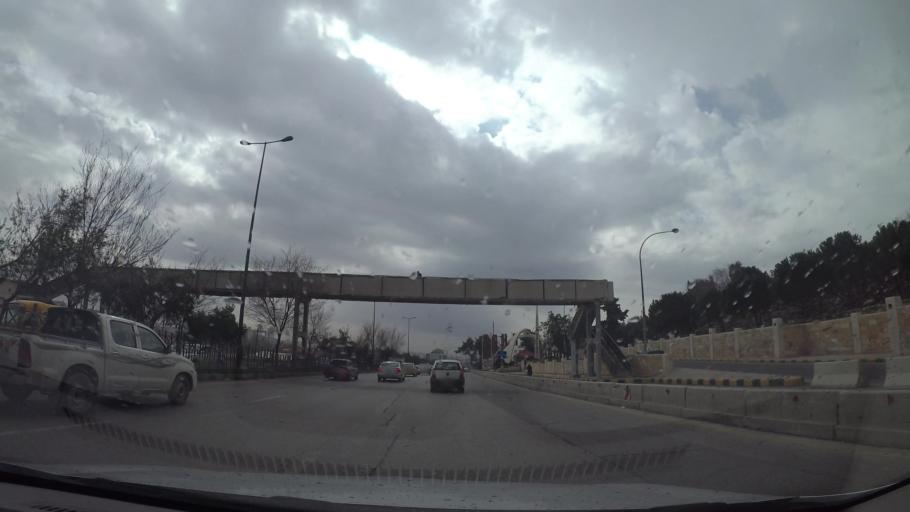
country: JO
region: Amman
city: Wadi as Sir
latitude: 31.9797
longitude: 35.8356
